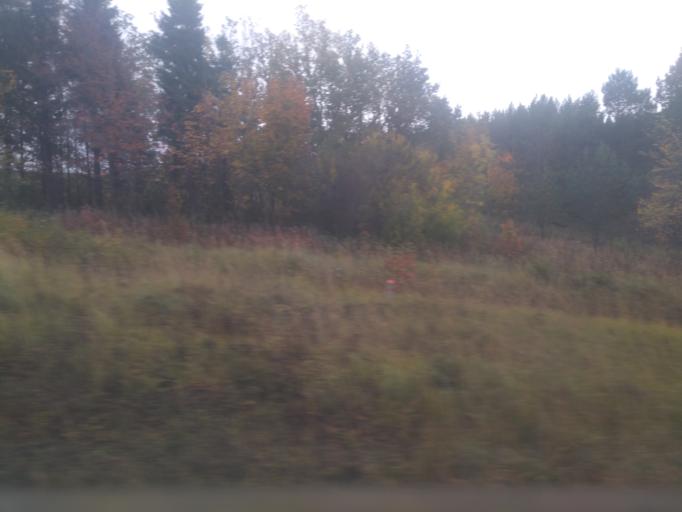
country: RU
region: Udmurtiya
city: Alnashi
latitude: 56.2342
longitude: 52.7219
